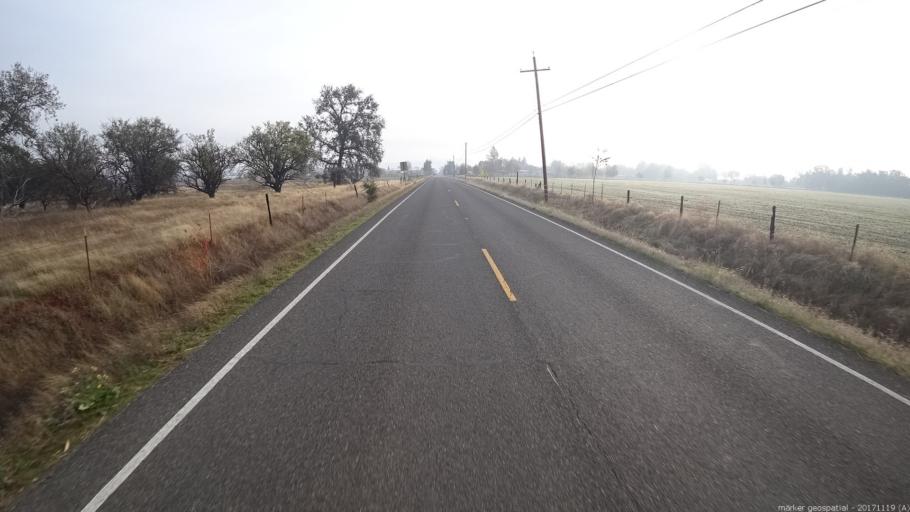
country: US
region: California
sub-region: Shasta County
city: Anderson
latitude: 40.4804
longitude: -122.2784
